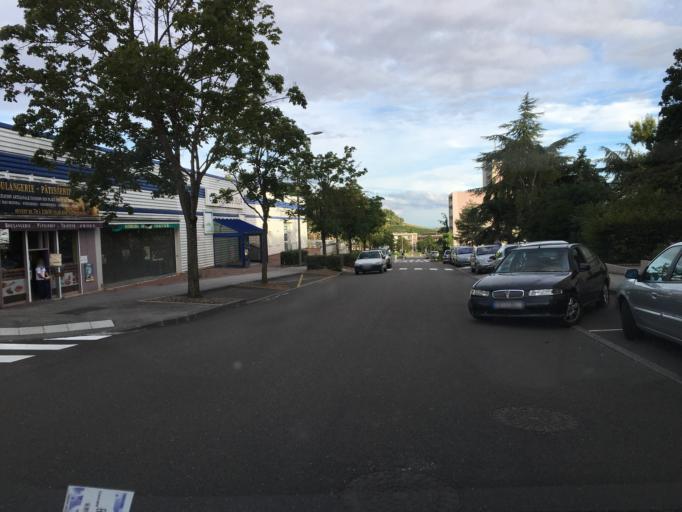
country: FR
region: Bourgogne
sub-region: Departement de la Cote-d'Or
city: Daix
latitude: 47.3404
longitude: 4.9945
